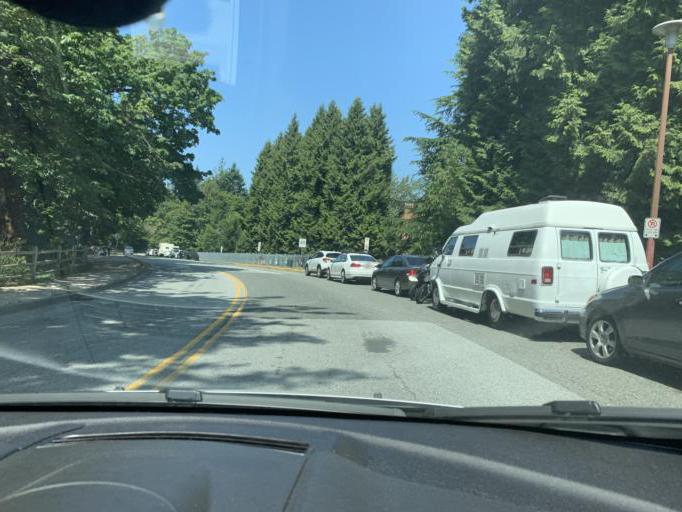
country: CA
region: British Columbia
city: West End
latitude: 49.2631
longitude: -123.2586
